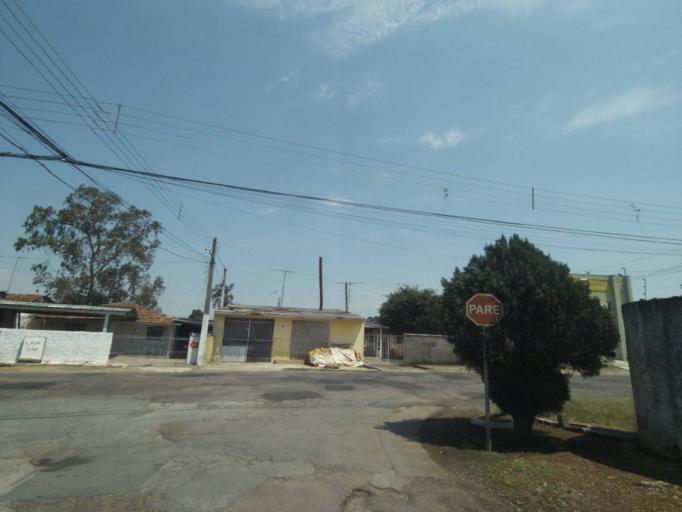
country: BR
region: Parana
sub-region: Sao Jose Dos Pinhais
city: Sao Jose dos Pinhais
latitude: -25.5204
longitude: -49.2687
